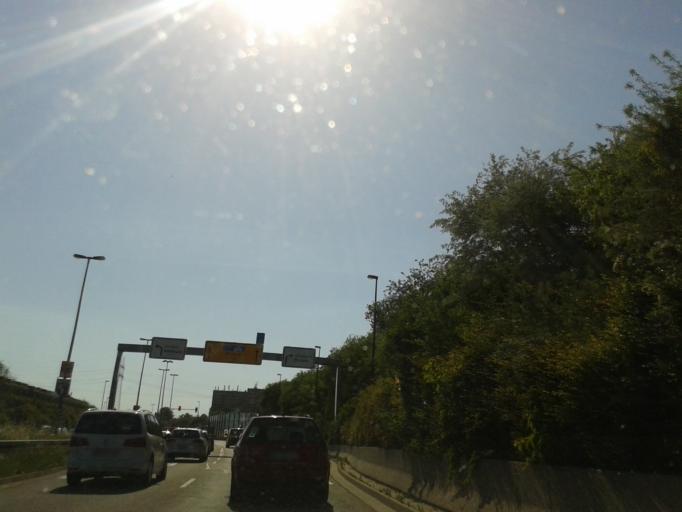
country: DE
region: Saxony
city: Freital
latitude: 51.0489
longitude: 13.6575
